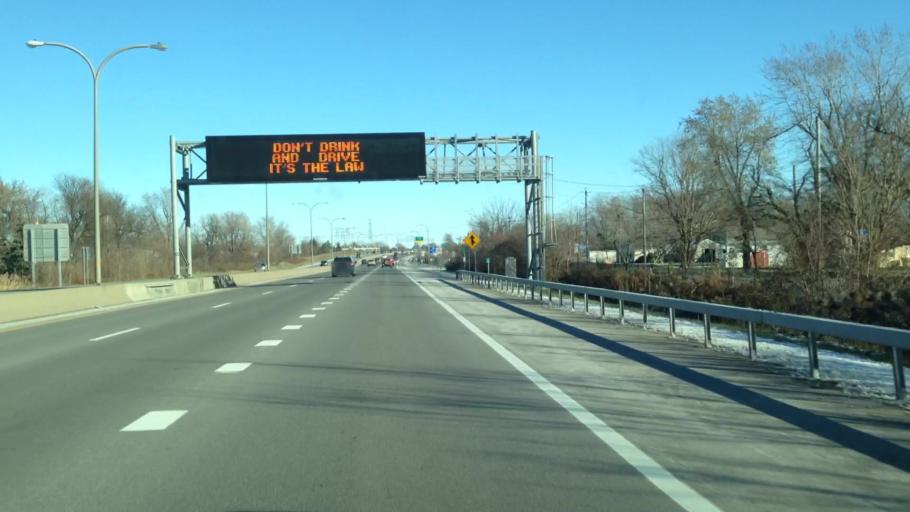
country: US
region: New York
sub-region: Erie County
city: Cheektowaga
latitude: 42.9329
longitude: -78.7796
